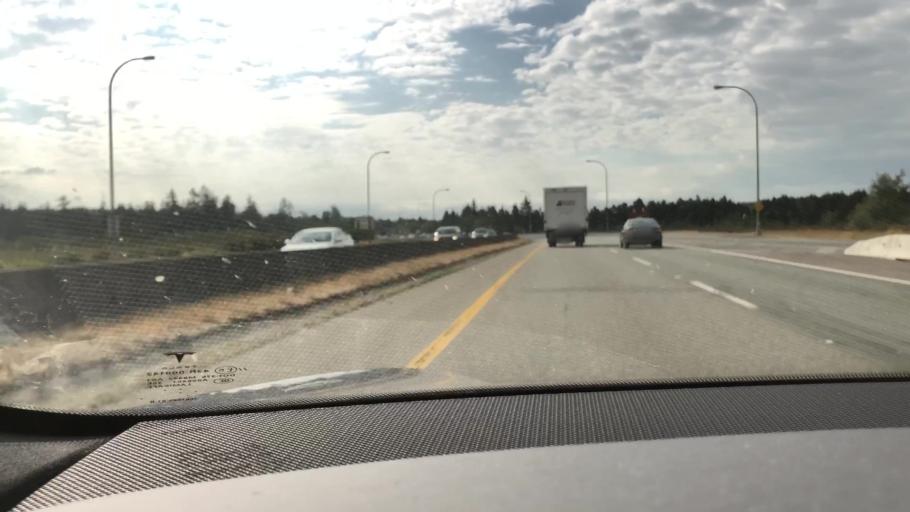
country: CA
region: British Columbia
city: Delta
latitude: 49.1427
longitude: -122.9359
